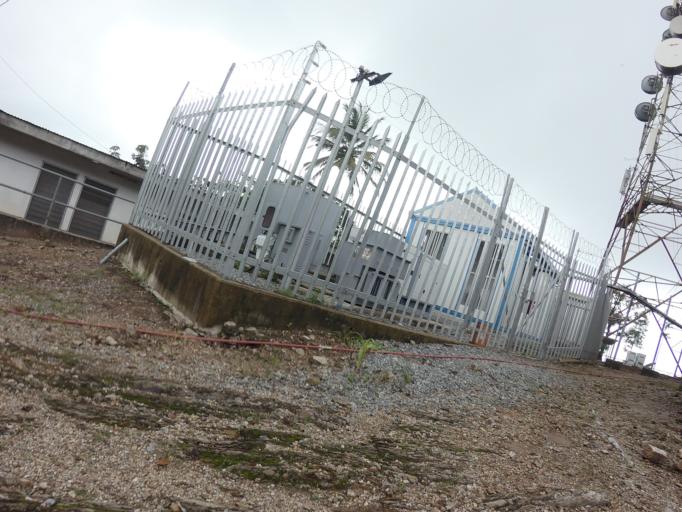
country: GH
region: Volta
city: Kpandu
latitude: 6.8391
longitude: 0.4306
